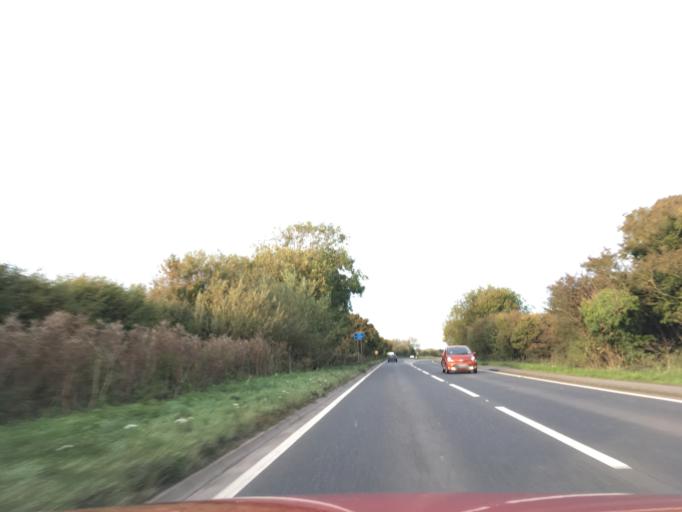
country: GB
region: England
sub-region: South Gloucestershire
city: Severn Beach
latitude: 51.5860
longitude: -2.6357
